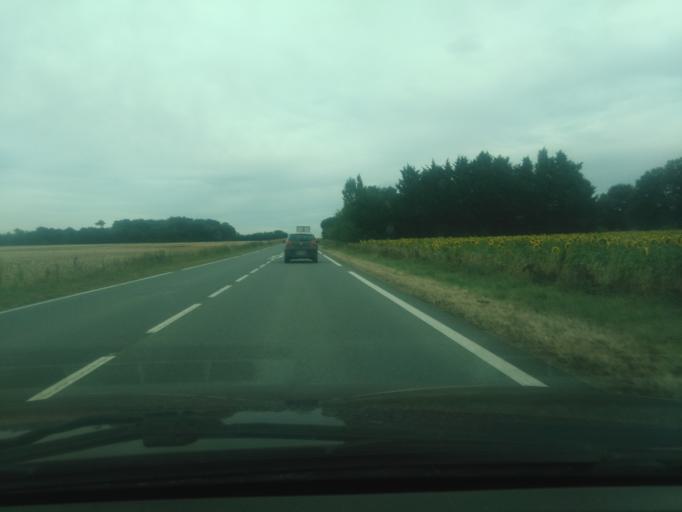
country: FR
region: Poitou-Charentes
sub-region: Departement de la Vienne
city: Saint-Savin
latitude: 46.5727
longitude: 0.8106
